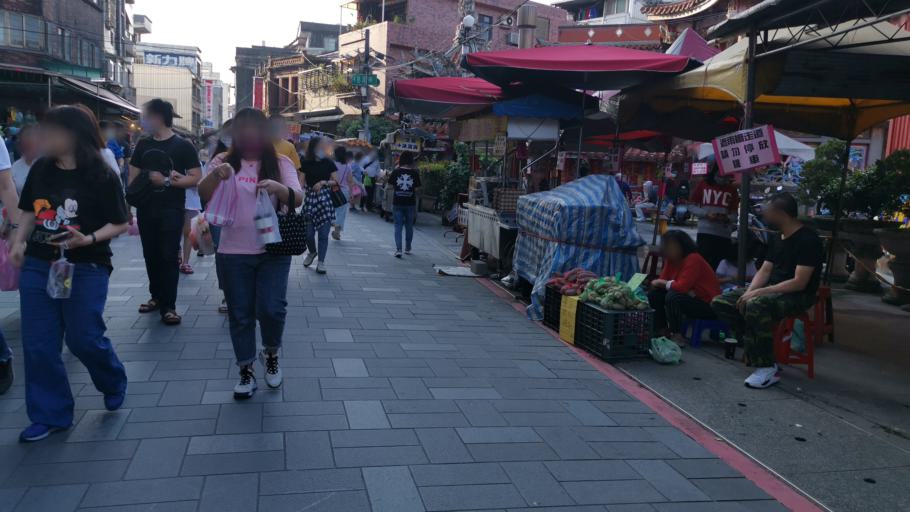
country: TW
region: Taiwan
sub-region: Keelung
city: Keelung
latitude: 25.2206
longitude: 121.6403
